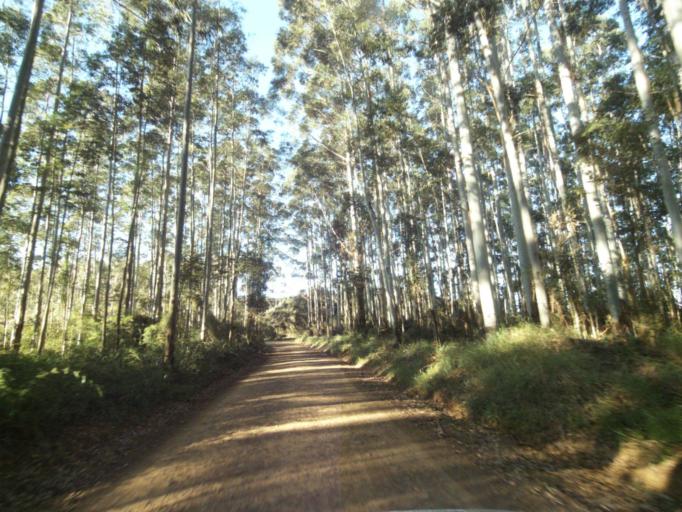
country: BR
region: Parana
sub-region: Telemaco Borba
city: Telemaco Borba
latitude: -24.5063
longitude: -50.5999
